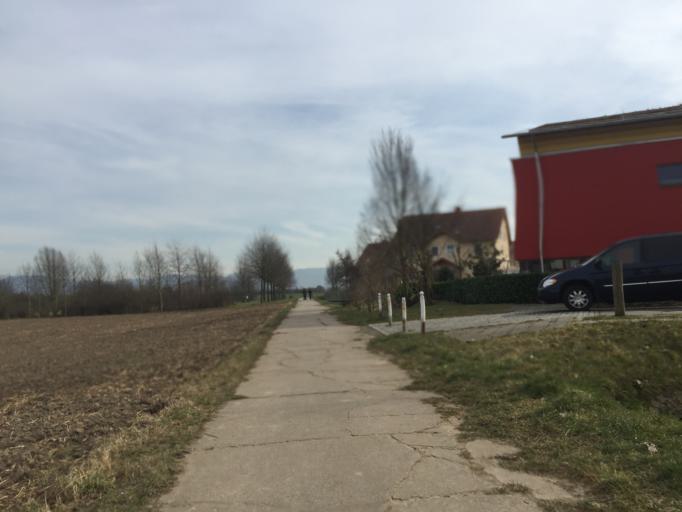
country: DE
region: Hesse
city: Viernheim
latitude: 49.5488
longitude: 8.6009
